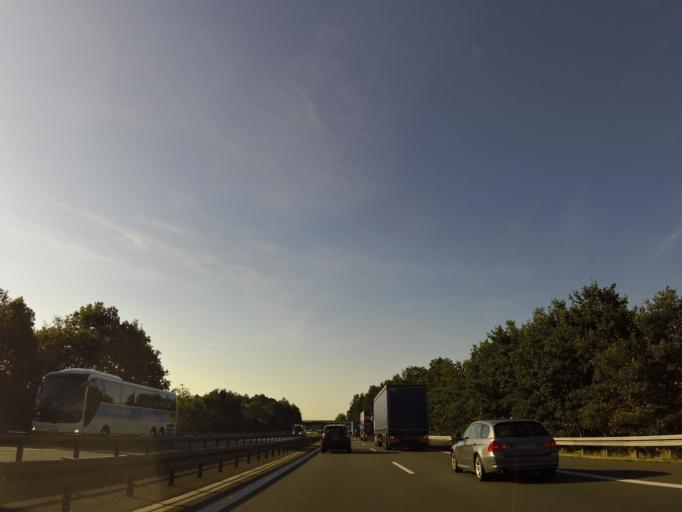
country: DE
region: Bavaria
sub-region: Regierungsbezirk Mittelfranken
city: Hessdorf
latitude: 49.6530
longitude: 10.8989
